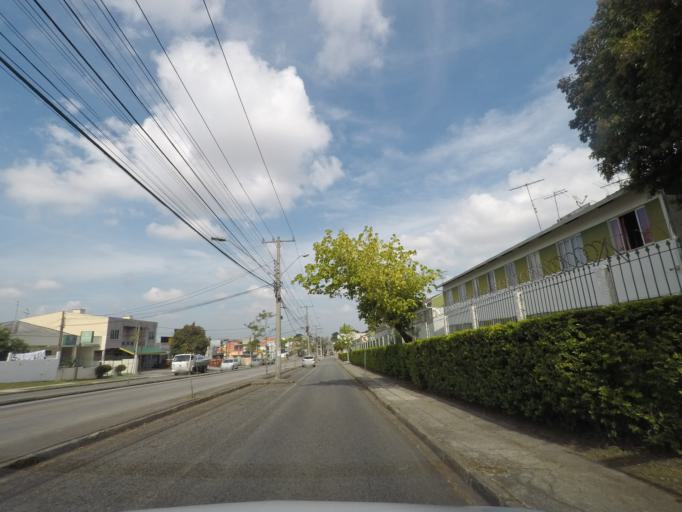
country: BR
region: Parana
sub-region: Pinhais
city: Pinhais
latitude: -25.4558
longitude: -49.2136
